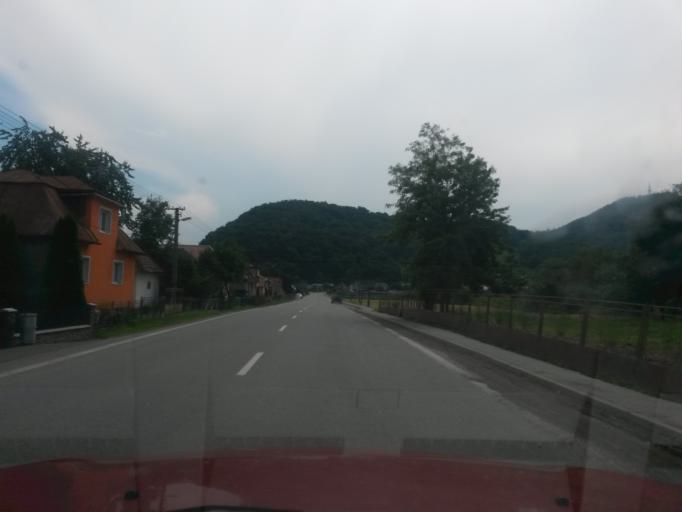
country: SK
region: Presovsky
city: Snina
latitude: 48.9956
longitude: 22.2181
